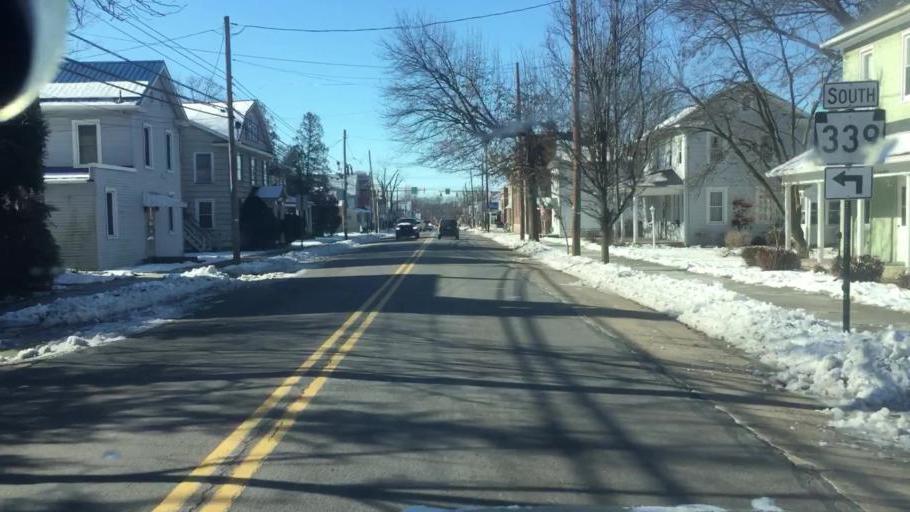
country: US
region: Pennsylvania
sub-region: Luzerne County
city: Nescopeck
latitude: 41.0523
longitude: -76.2193
